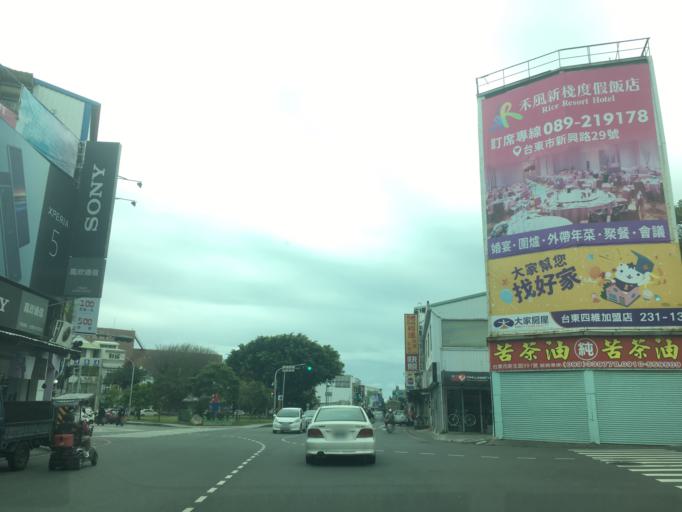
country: TW
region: Taiwan
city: Taitung City
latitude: 22.7575
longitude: 121.1427
